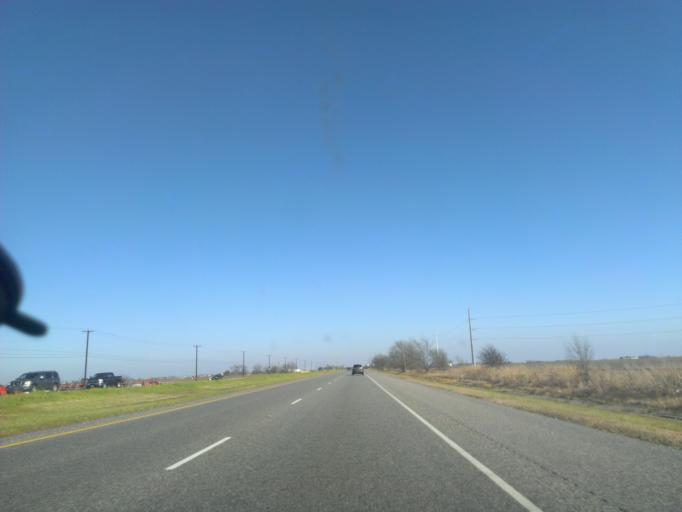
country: US
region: Texas
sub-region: Williamson County
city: Taylor
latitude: 30.5781
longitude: -97.3649
